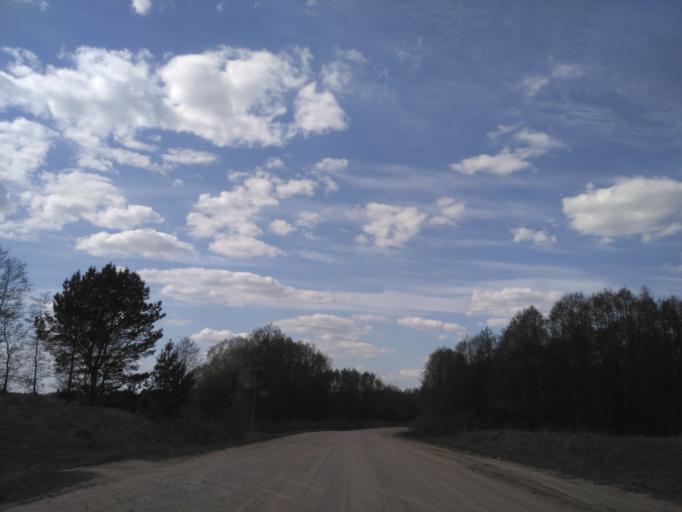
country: BY
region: Minsk
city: Narach
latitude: 54.9952
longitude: 26.5600
